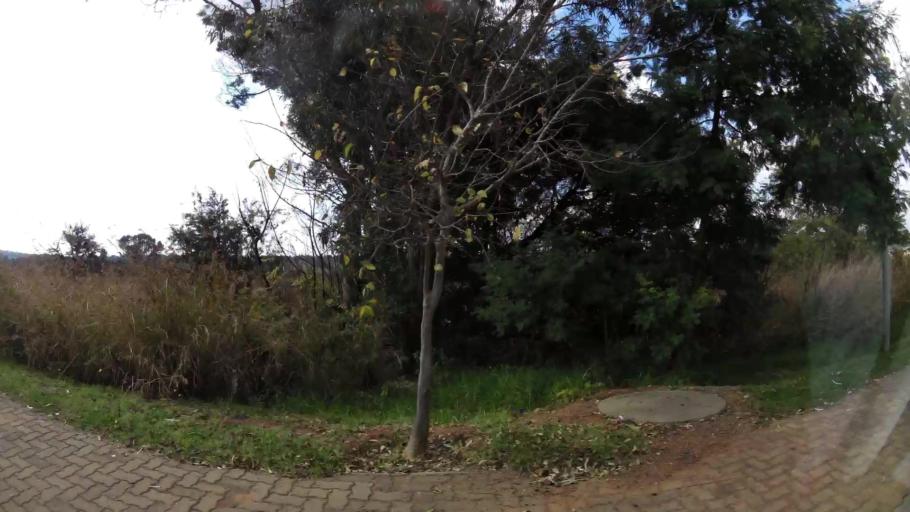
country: ZA
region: Gauteng
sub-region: City of Tshwane Metropolitan Municipality
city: Centurion
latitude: -25.8237
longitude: 28.2440
